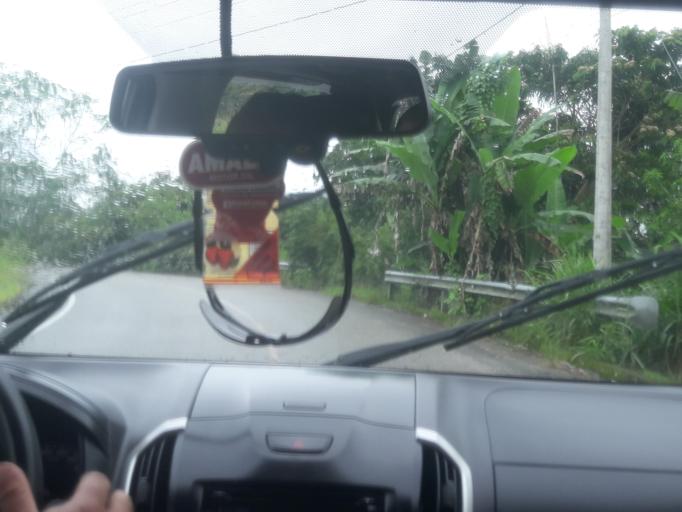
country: EC
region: Napo
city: Tena
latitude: -1.0409
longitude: -77.6962
